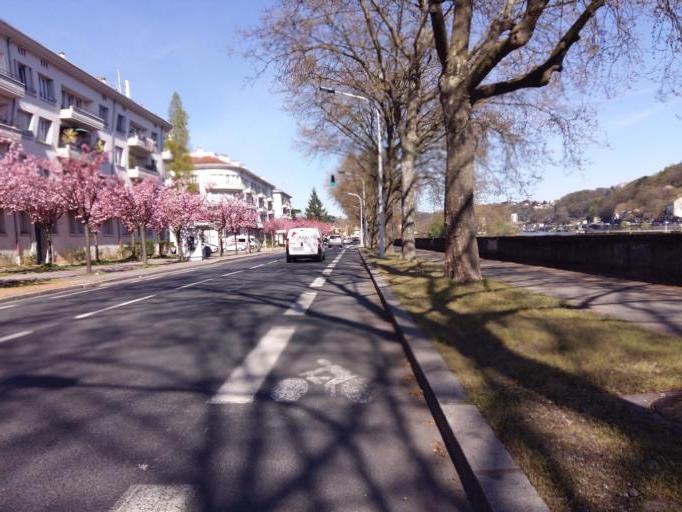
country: FR
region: Rhone-Alpes
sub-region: Departement du Rhone
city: Caluire-et-Cuire
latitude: 45.7947
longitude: 4.8241
